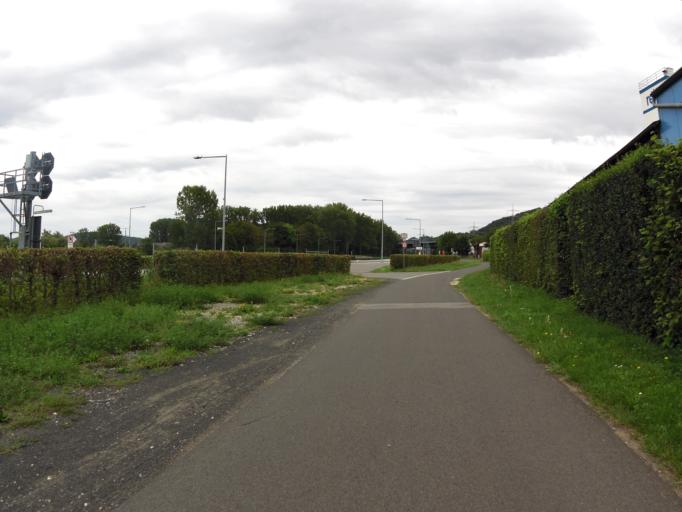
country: DE
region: Bavaria
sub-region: Regierungsbezirk Unterfranken
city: Eltmann
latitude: 49.9800
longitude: 10.6406
